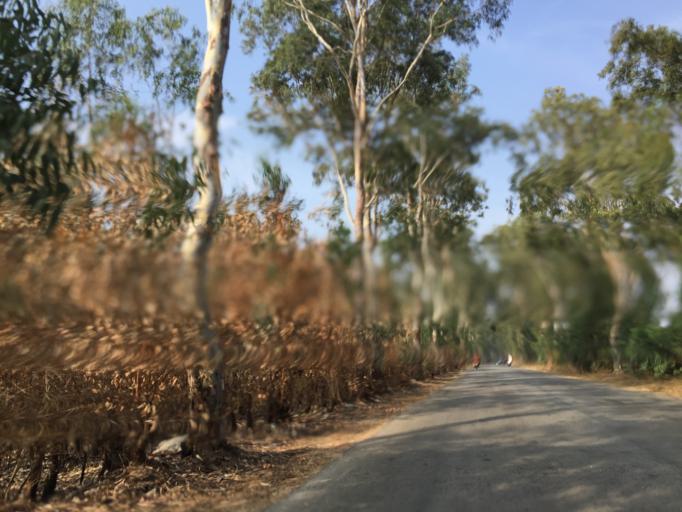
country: IN
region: Karnataka
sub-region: Chikkaballapur
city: Chik Ballapur
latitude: 13.3472
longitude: 77.6794
